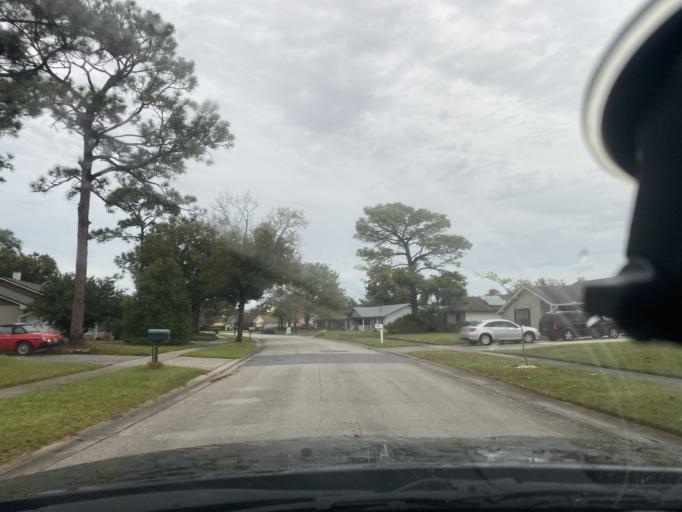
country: US
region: Florida
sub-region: Orange County
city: Azalea Park
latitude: 28.5355
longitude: -81.2631
